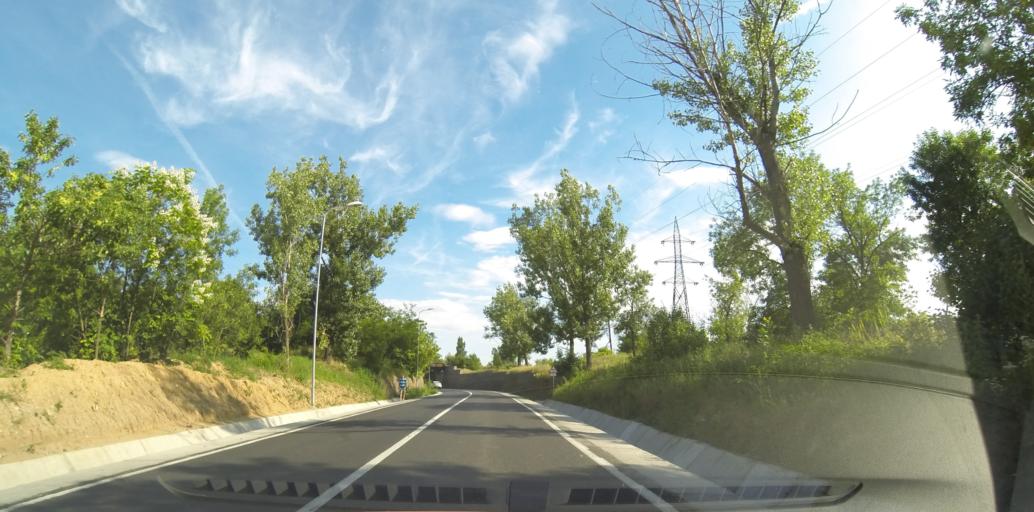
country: RO
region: Dolj
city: Craiova
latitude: 44.3436
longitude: 23.7888
